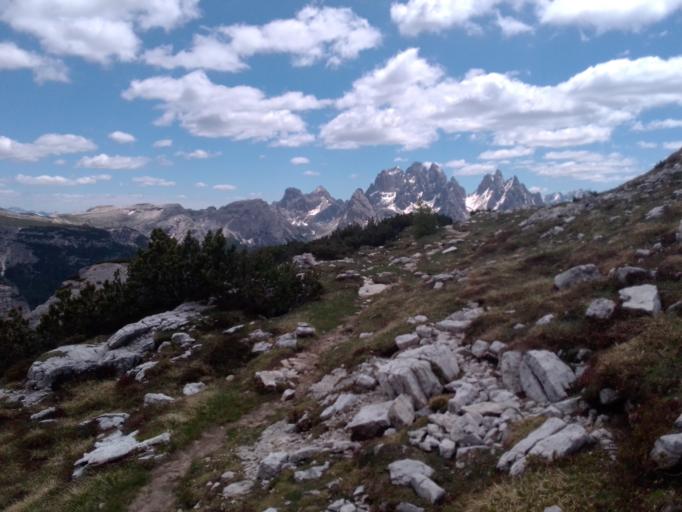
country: IT
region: Trentino-Alto Adige
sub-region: Bolzano
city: Dobbiaco
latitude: 46.6239
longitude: 12.2474
